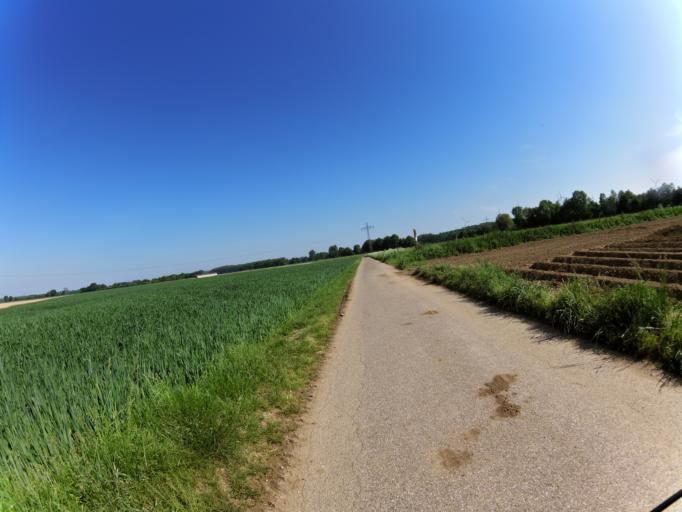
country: DE
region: North Rhine-Westphalia
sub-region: Regierungsbezirk Koln
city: Linnich
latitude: 51.0003
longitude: 6.2683
